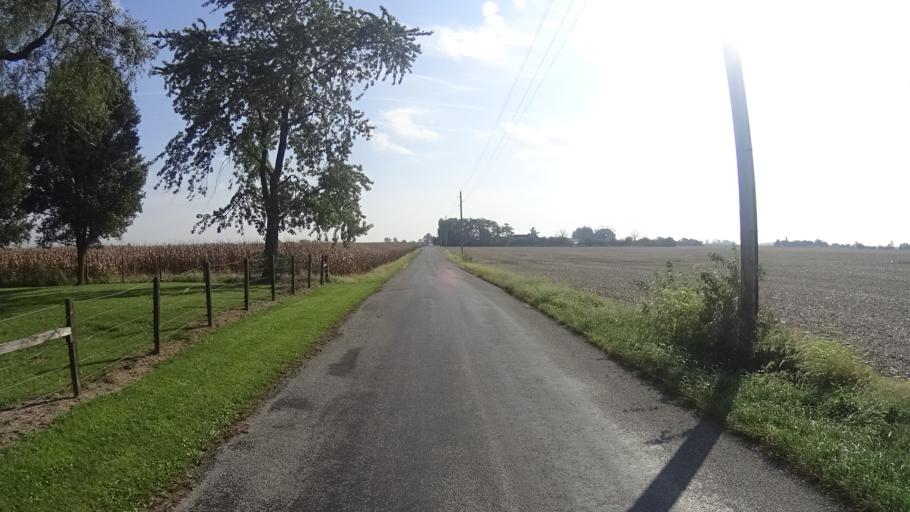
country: US
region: Indiana
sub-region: Madison County
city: Lapel
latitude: 40.0456
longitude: -85.8332
